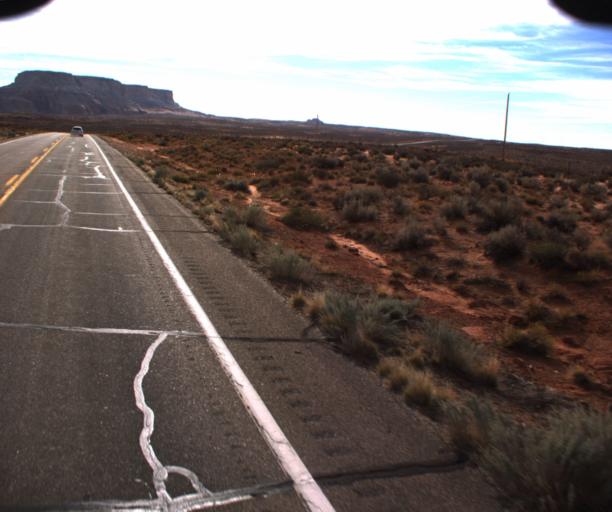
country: US
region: Arizona
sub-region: Coconino County
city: LeChee
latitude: 36.8805
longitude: -111.3484
